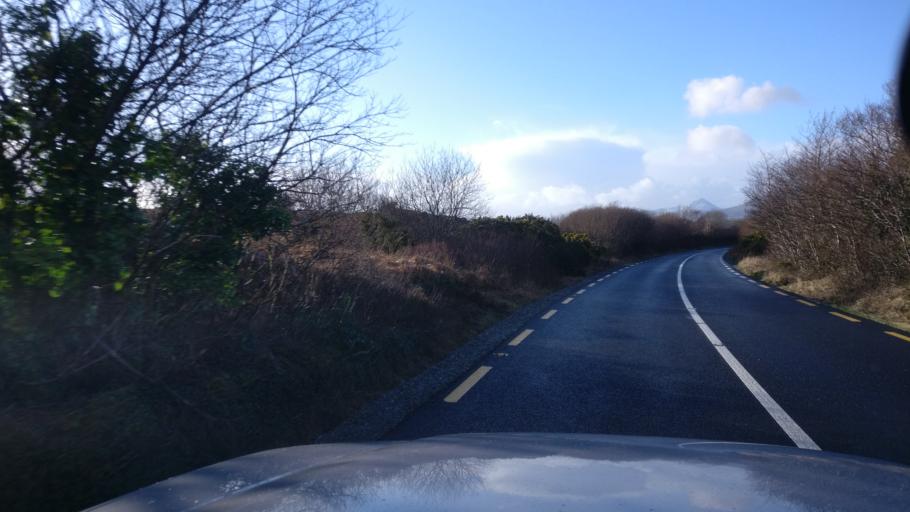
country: IE
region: Connaught
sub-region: County Galway
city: Oughterard
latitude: 53.4537
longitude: -9.6554
